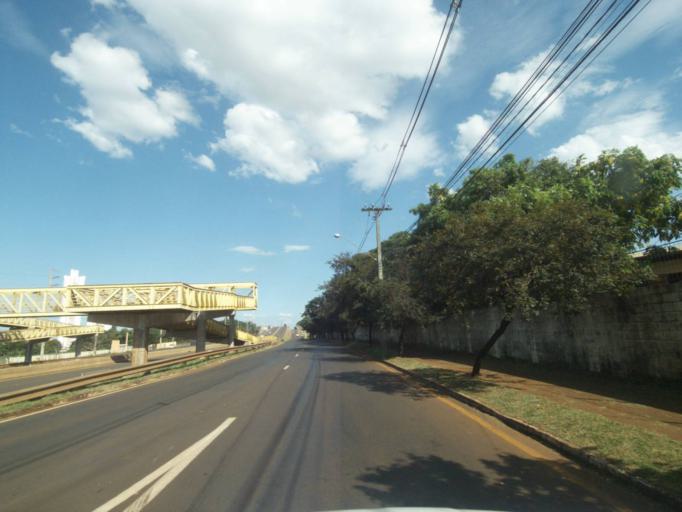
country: BR
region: Parana
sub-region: Londrina
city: Londrina
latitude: -23.3448
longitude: -51.1781
